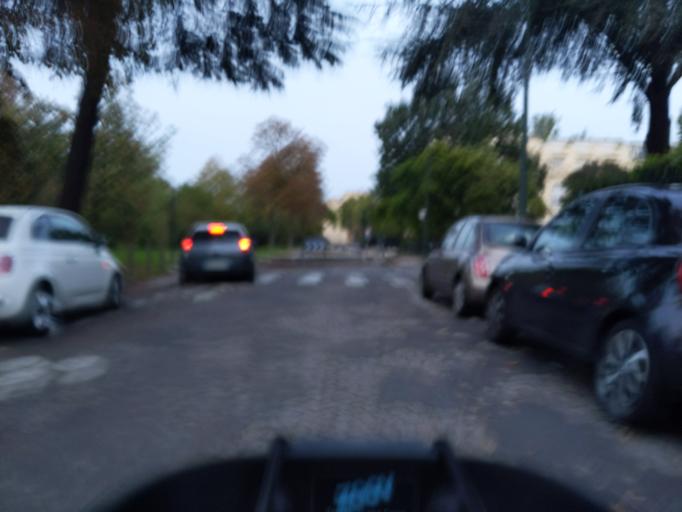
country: FR
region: Ile-de-France
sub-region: Departement des Hauts-de-Seine
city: Neuilly-sur-Seine
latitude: 48.8593
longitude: 2.2646
